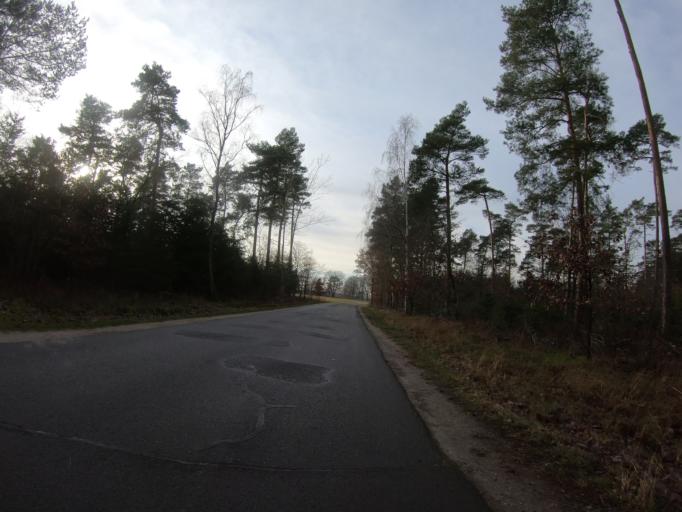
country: DE
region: Lower Saxony
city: Meinersen
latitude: 52.4874
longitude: 10.3880
